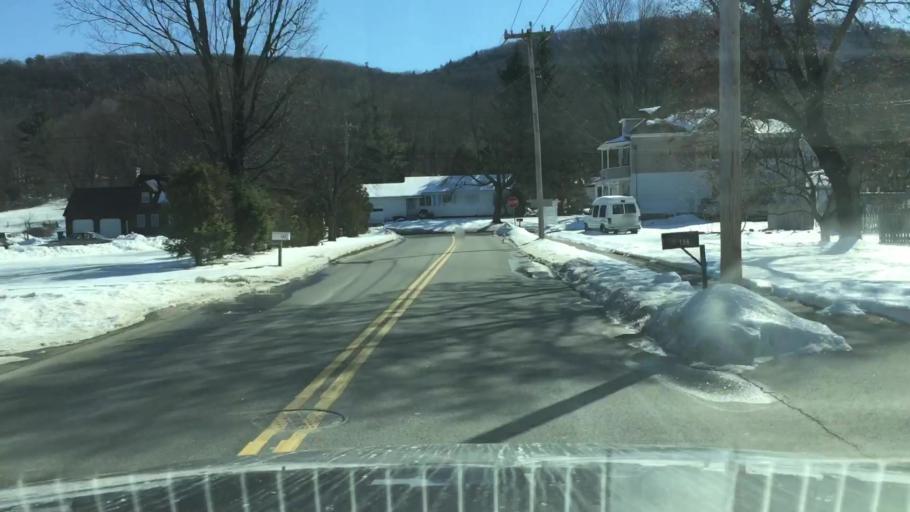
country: US
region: Massachusetts
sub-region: Hampshire County
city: Easthampton
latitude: 42.2690
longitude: -72.6479
